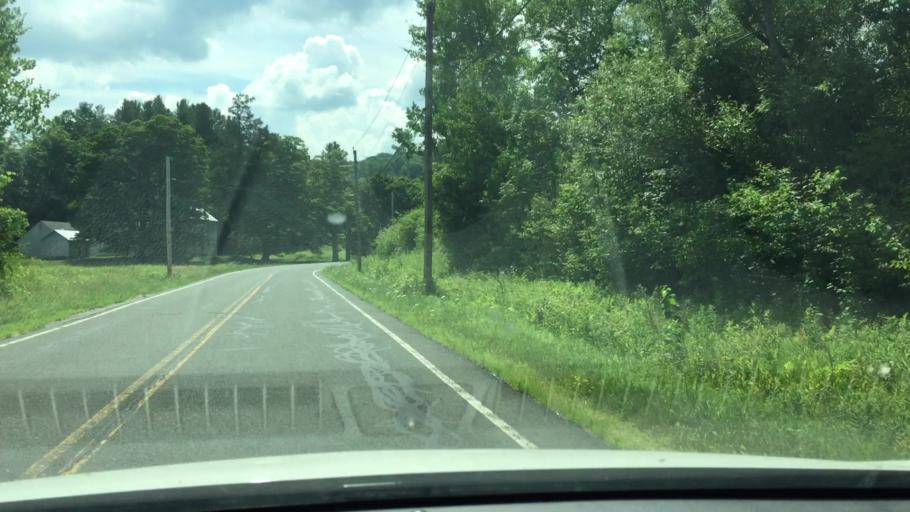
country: US
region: Massachusetts
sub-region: Berkshire County
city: Otis
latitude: 42.2177
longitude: -73.1800
